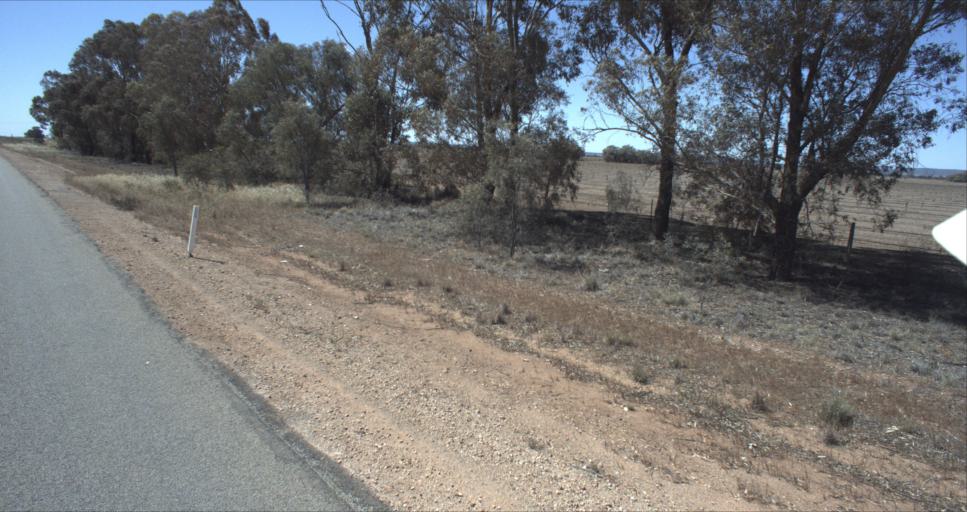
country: AU
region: New South Wales
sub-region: Leeton
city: Leeton
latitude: -34.5131
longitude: 146.3450
